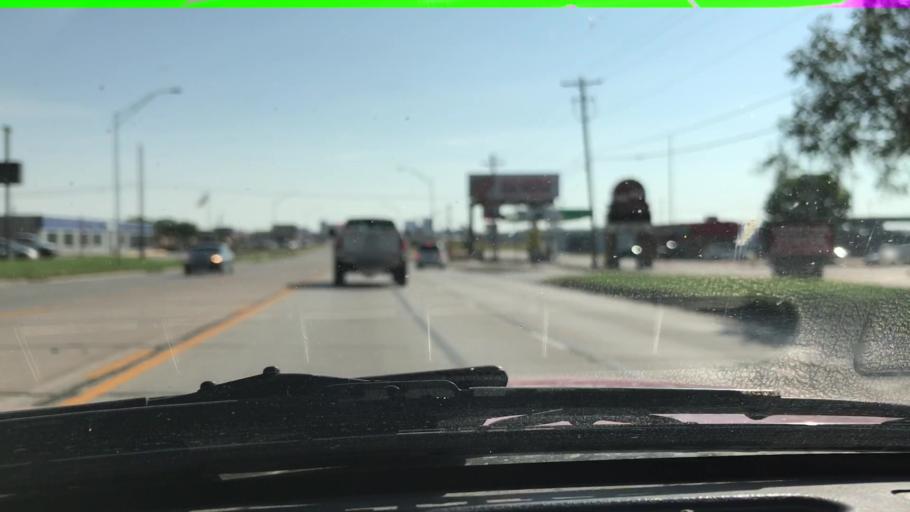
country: US
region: Nebraska
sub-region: Lancaster County
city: Lincoln
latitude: 40.8137
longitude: -96.7375
